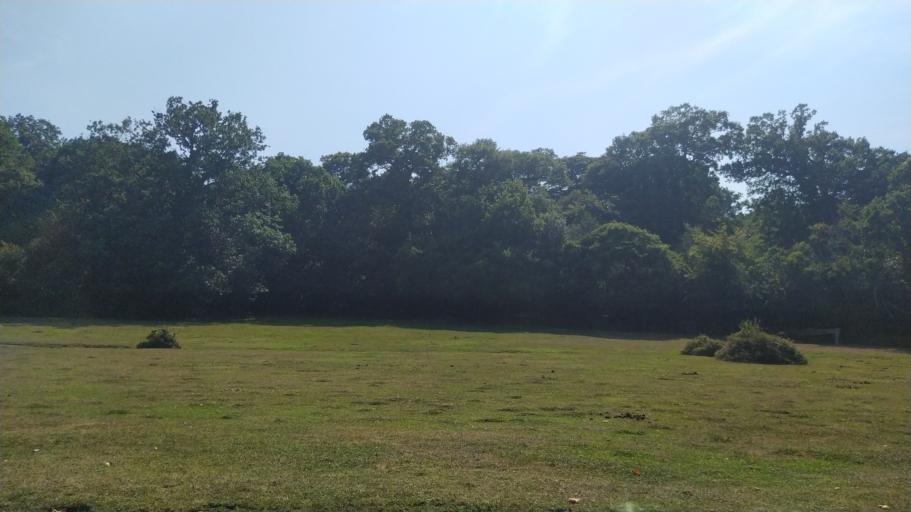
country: GB
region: England
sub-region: Hampshire
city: Cadnam
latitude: 50.8998
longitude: -1.5431
